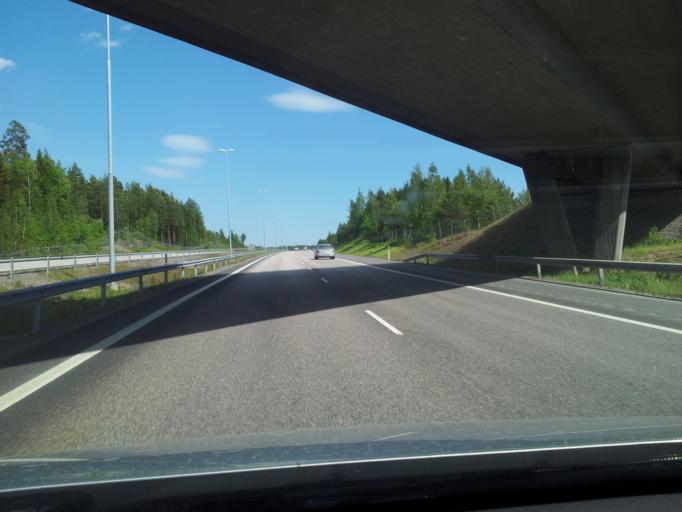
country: FI
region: Uusimaa
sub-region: Loviisa
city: Perna
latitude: 60.4915
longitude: 25.9796
